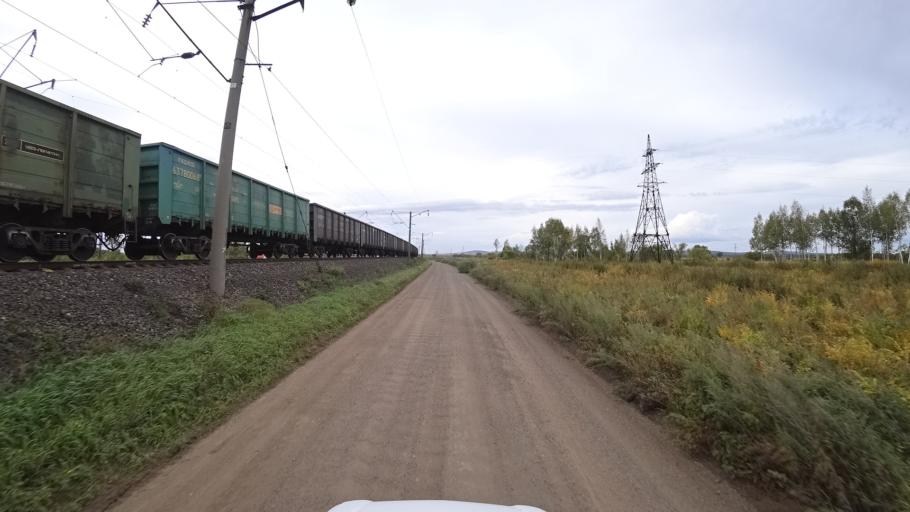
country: RU
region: Amur
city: Arkhara
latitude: 49.3684
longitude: 130.1421
